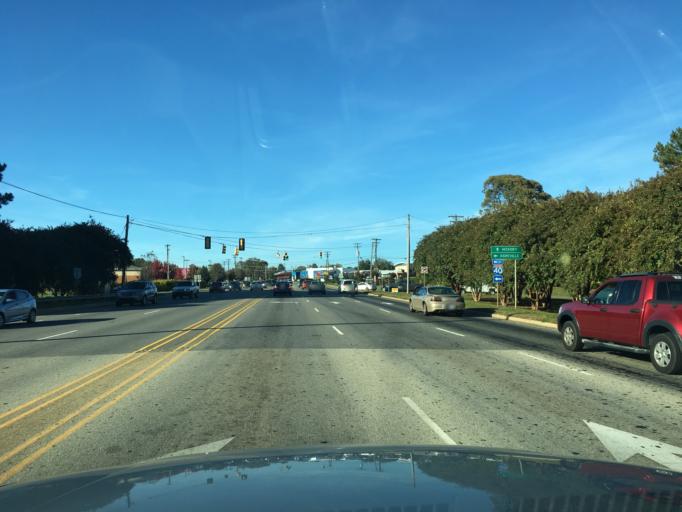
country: US
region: North Carolina
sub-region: Catawba County
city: Hickory
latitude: 35.7139
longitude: -81.3130
